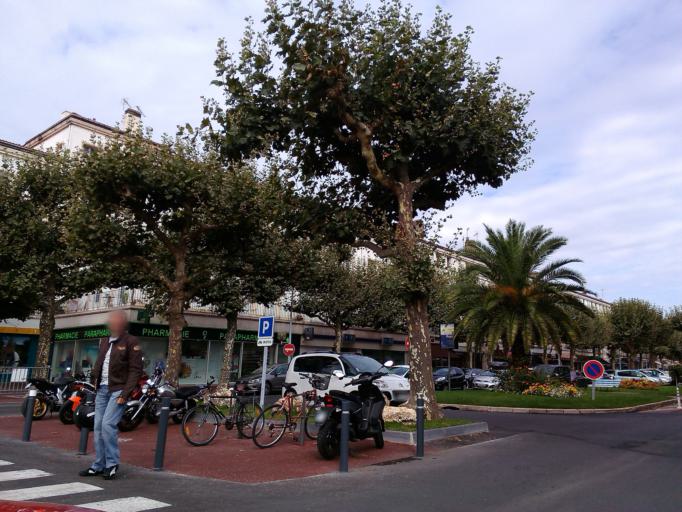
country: FR
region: Poitou-Charentes
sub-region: Departement de la Charente-Maritime
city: Royan
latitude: 45.6249
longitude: -1.0289
